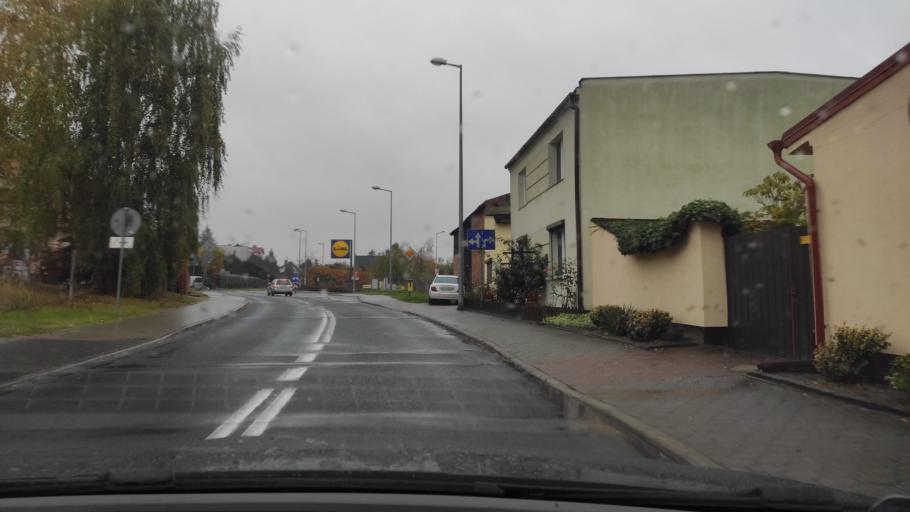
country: PL
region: Greater Poland Voivodeship
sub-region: Powiat poznanski
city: Kornik
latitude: 52.2542
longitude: 17.0838
